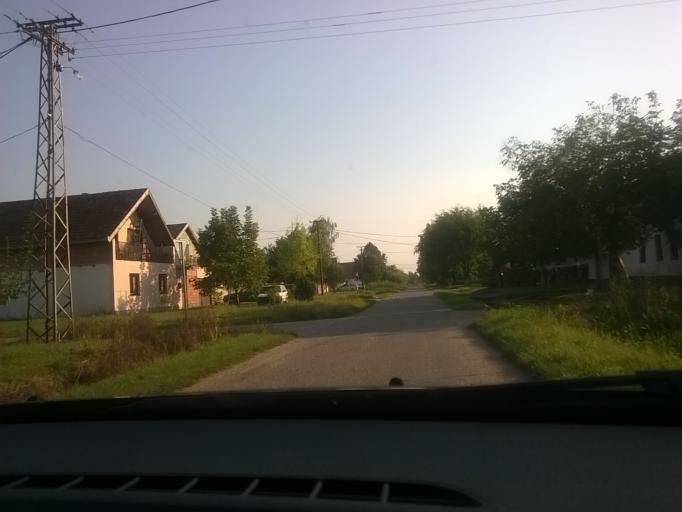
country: RS
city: Pavlis
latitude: 45.1053
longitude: 21.2434
